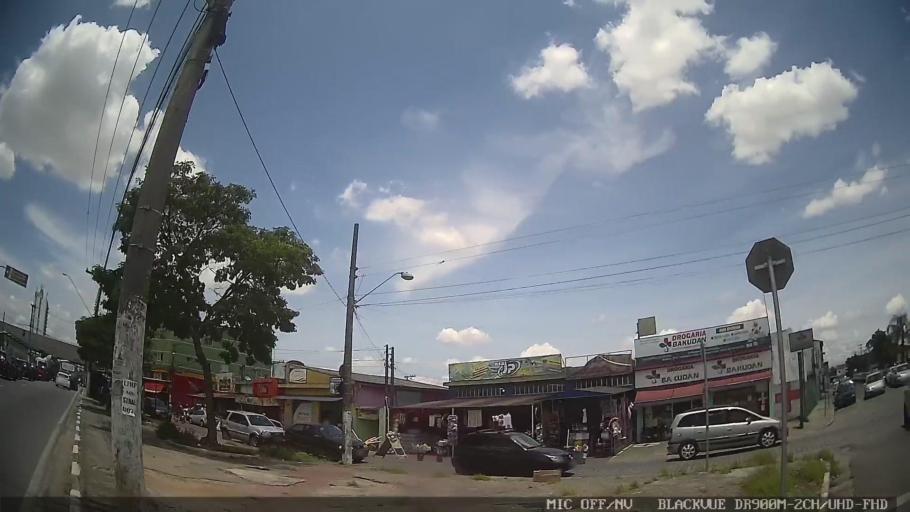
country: BR
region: Sao Paulo
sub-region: Suzano
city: Suzano
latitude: -23.5322
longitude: -46.3071
